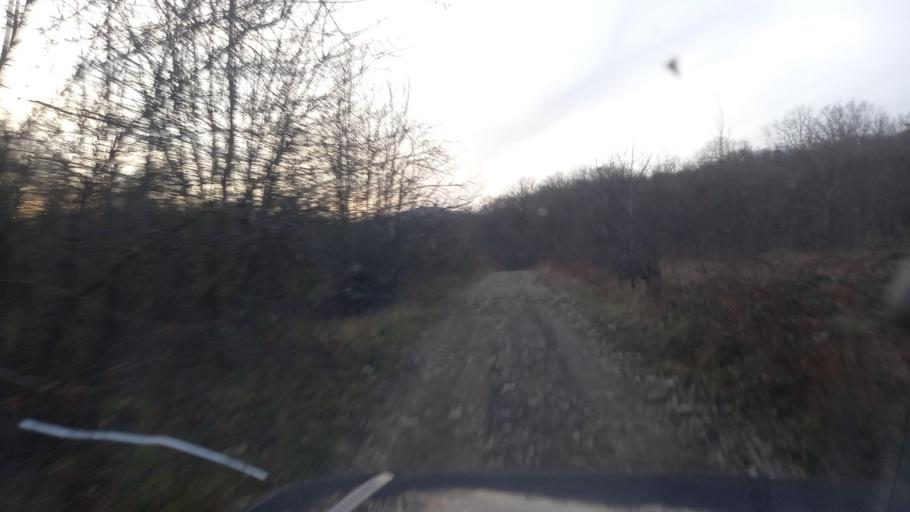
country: RU
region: Krasnodarskiy
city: Goryachiy Klyuch
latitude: 44.3818
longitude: 39.1503
